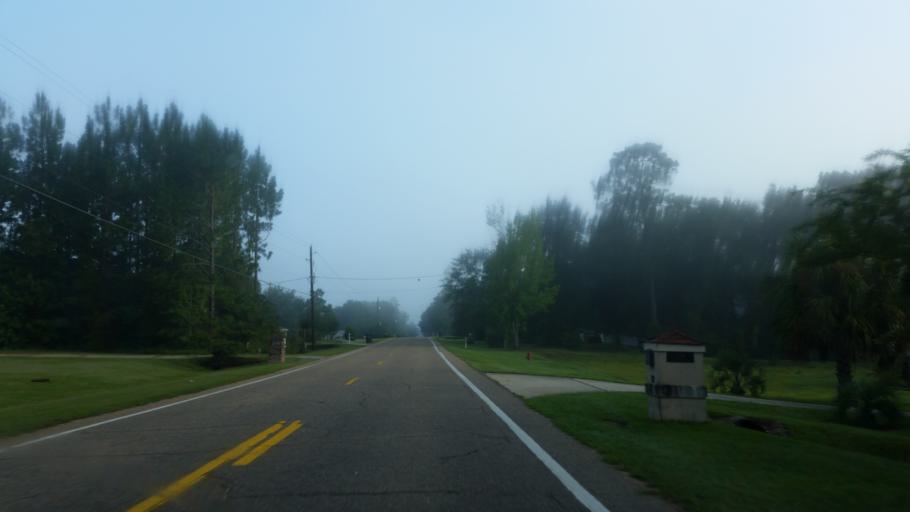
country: US
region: Florida
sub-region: Escambia County
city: Molino
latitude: 30.7329
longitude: -87.3454
